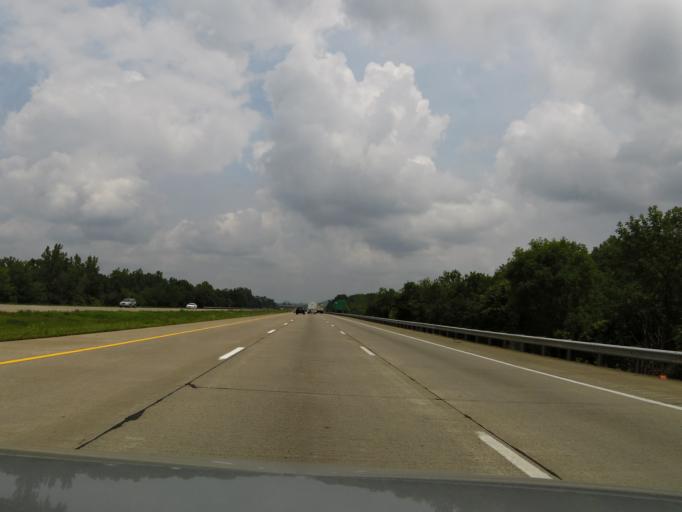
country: US
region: Kentucky
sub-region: Bullitt County
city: Lebanon Junction
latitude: 37.7955
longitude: -85.7534
